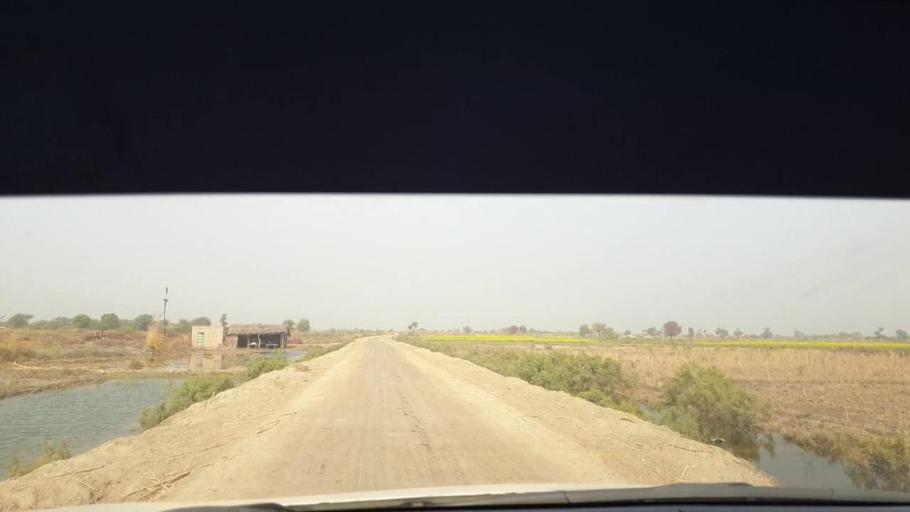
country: PK
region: Sindh
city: Berani
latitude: 25.8422
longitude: 68.8473
